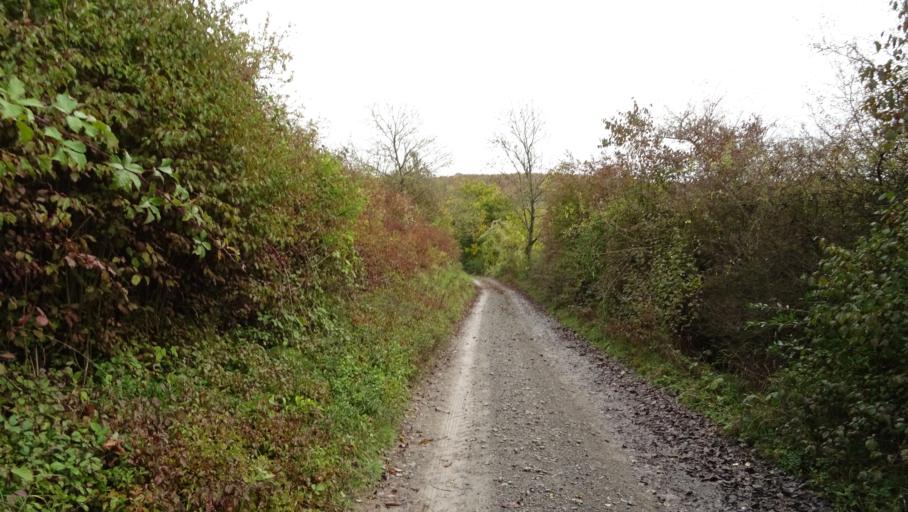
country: DE
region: Baden-Wuerttemberg
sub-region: Karlsruhe Region
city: Obrigheim
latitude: 49.3764
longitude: 9.0883
